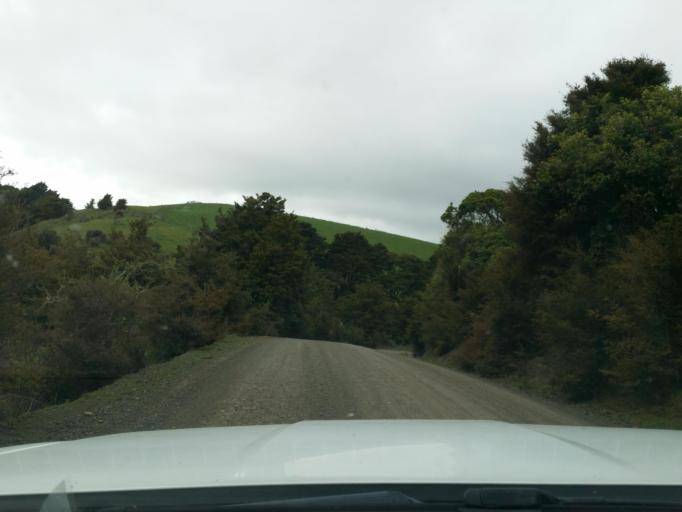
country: NZ
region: Northland
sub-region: Kaipara District
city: Dargaville
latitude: -35.7082
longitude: 173.6063
